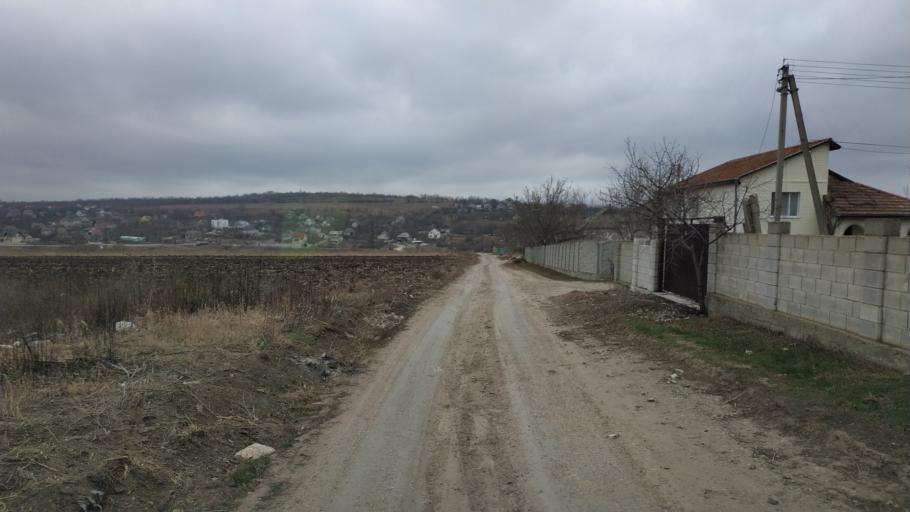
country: MD
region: Laloveni
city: Ialoveni
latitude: 46.9364
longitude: 28.7974
